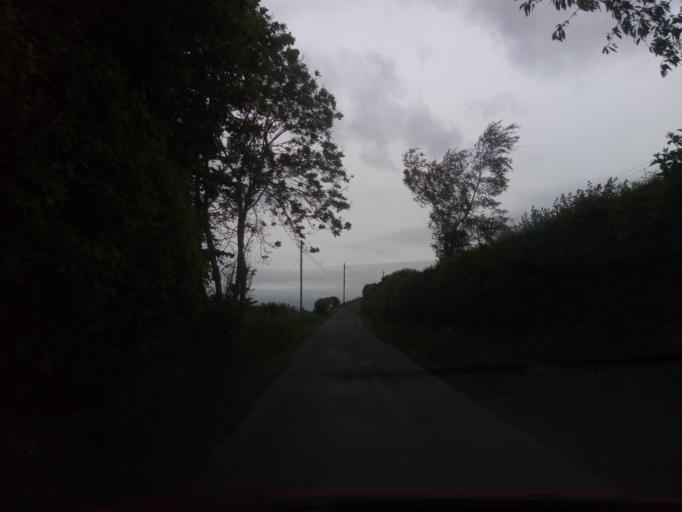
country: GB
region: Scotland
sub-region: The Scottish Borders
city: Selkirk
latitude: 55.5588
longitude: -2.8056
